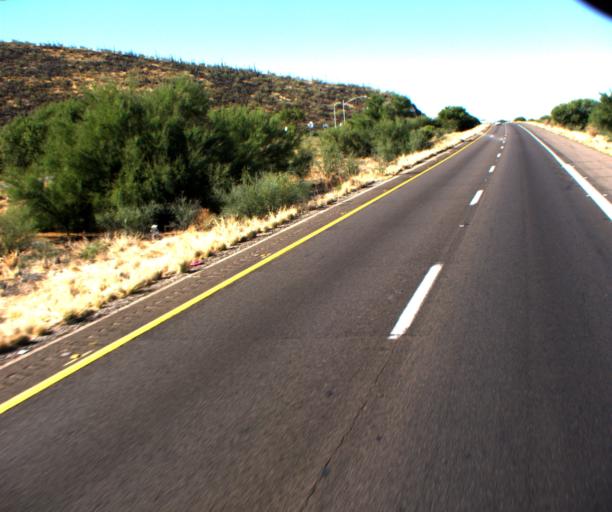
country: US
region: Arizona
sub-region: Pima County
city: Drexel Heights
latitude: 32.1108
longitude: -110.9921
